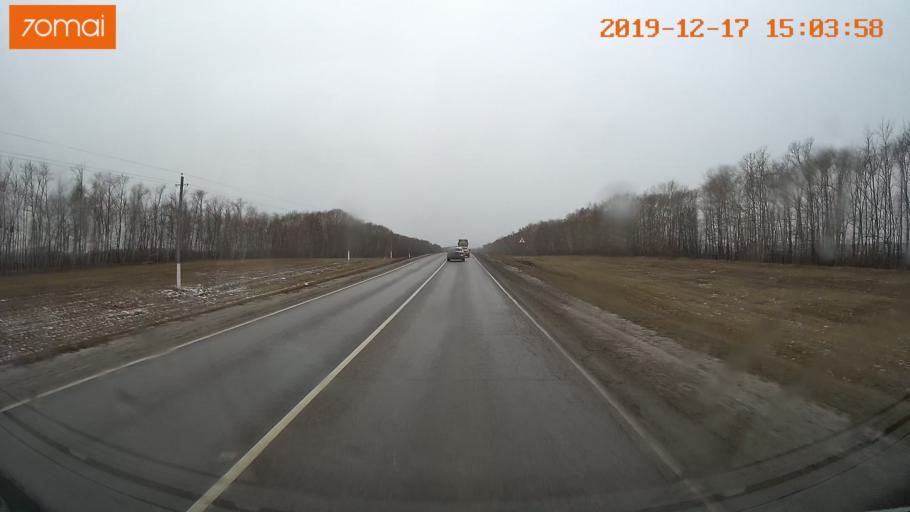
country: RU
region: Rjazan
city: Mikhaylov
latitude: 54.2665
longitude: 39.1436
